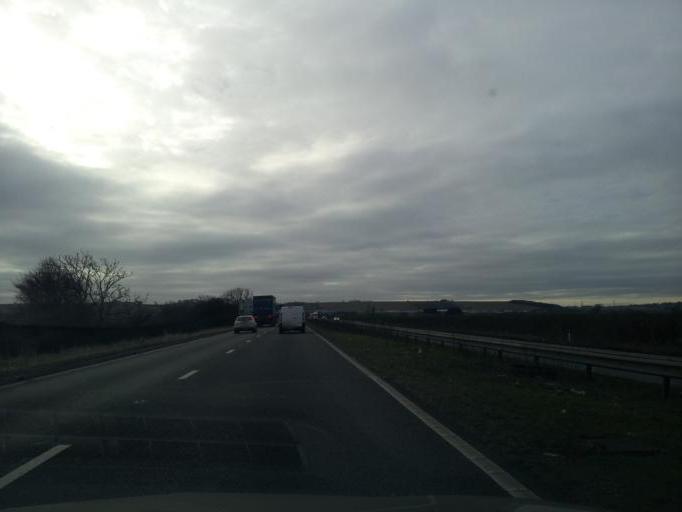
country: GB
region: England
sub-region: Lincolnshire
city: Great Gonerby
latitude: 52.9608
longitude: -0.6897
